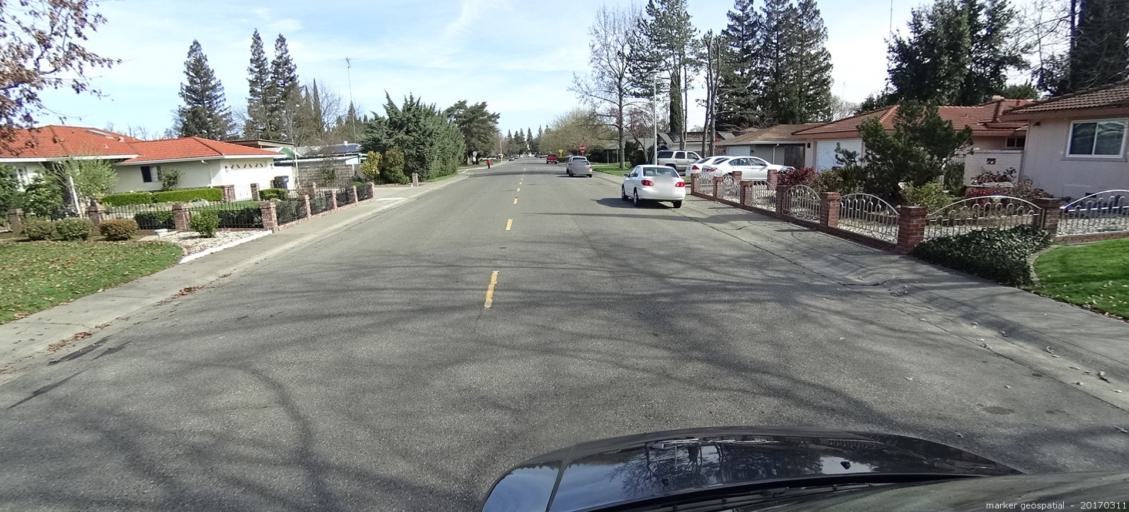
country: US
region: California
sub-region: Yolo County
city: West Sacramento
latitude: 38.5022
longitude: -121.5538
